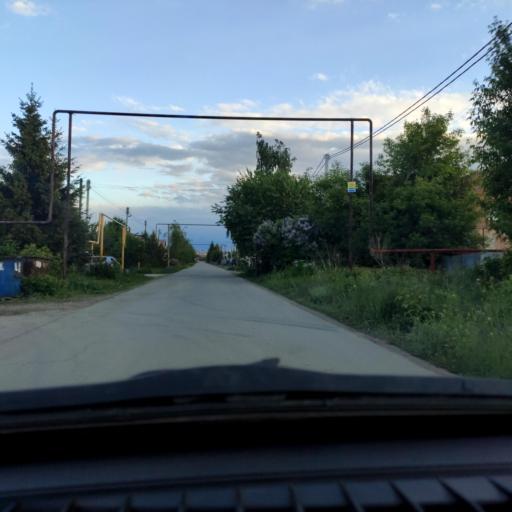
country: RU
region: Samara
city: Tol'yatti
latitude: 53.5602
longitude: 49.4022
